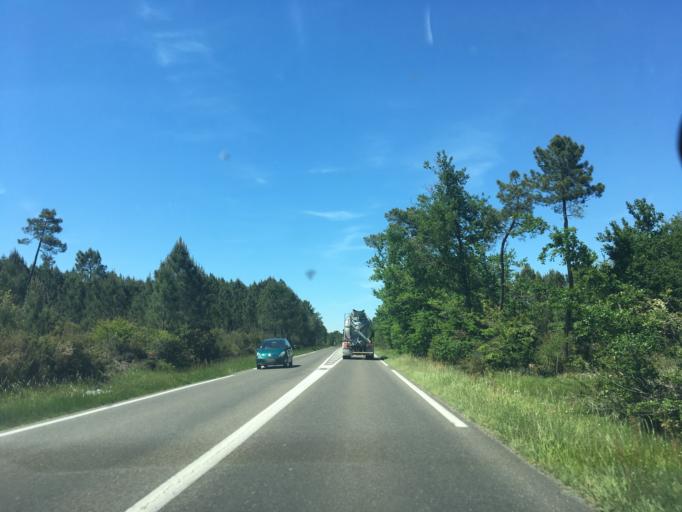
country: FR
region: Aquitaine
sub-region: Departement de la Gironde
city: Listrac-Medoc
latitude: 45.0980
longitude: -0.8011
